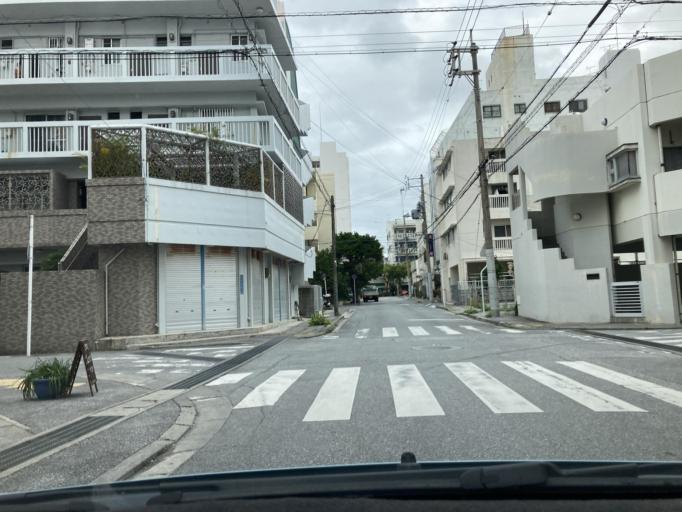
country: JP
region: Okinawa
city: Naha-shi
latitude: 26.2133
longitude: 127.6731
